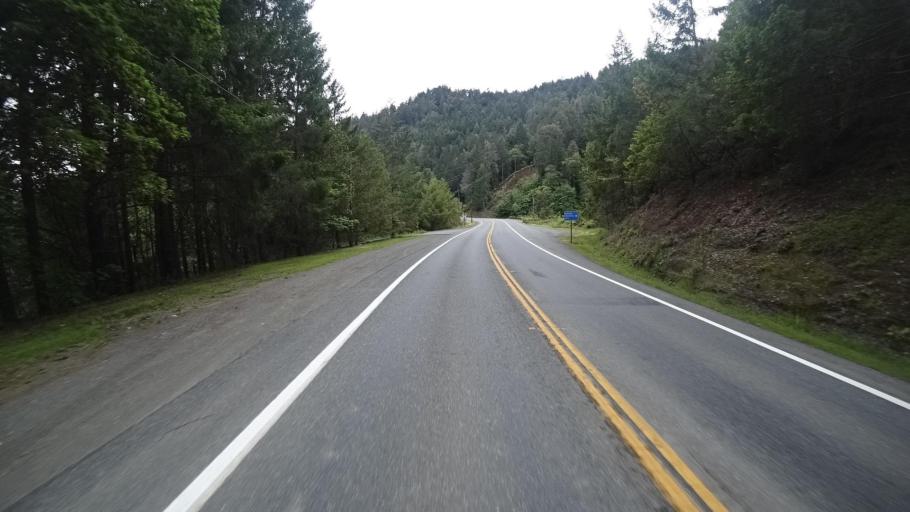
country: US
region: California
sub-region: Humboldt County
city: Willow Creek
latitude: 41.0010
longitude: -123.6471
